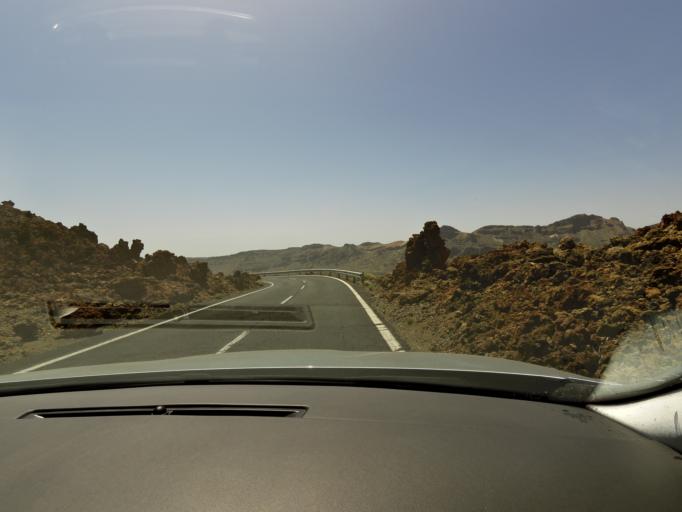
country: ES
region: Canary Islands
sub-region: Provincia de Santa Cruz de Tenerife
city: Vilaflor
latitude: 28.2593
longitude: -16.5998
